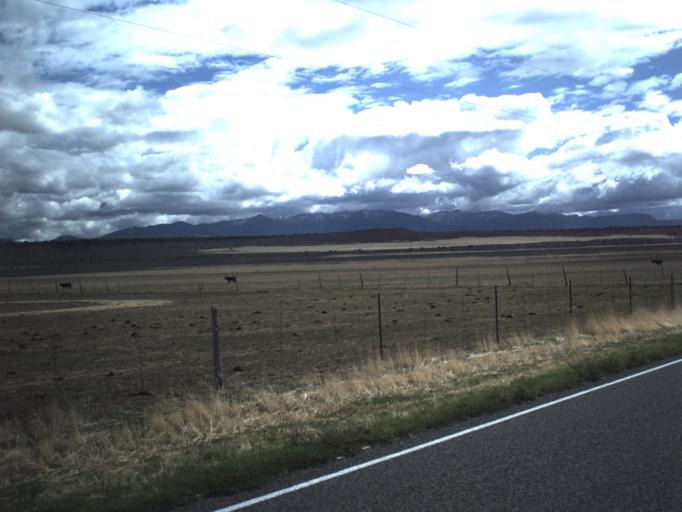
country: US
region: Utah
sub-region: Millard County
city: Fillmore
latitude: 39.0311
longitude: -112.4100
